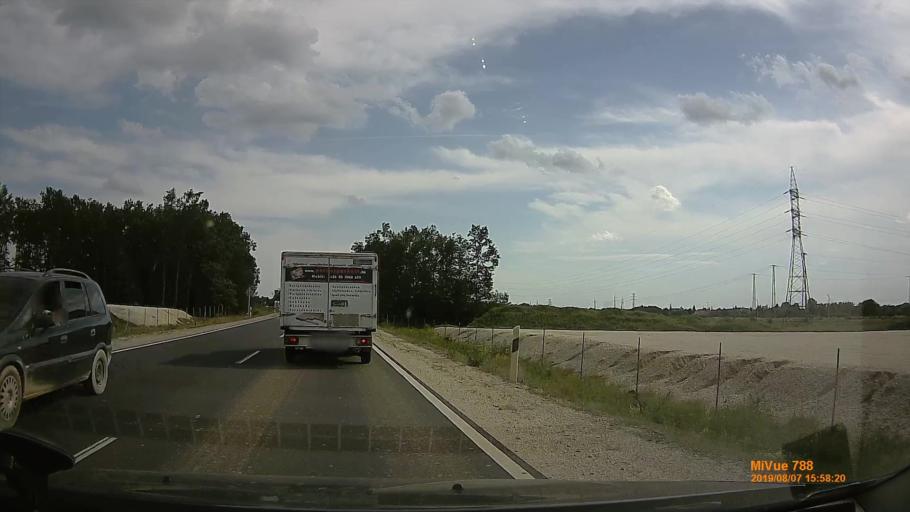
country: HU
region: Vas
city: Kormend
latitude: 47.0280
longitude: 16.6127
